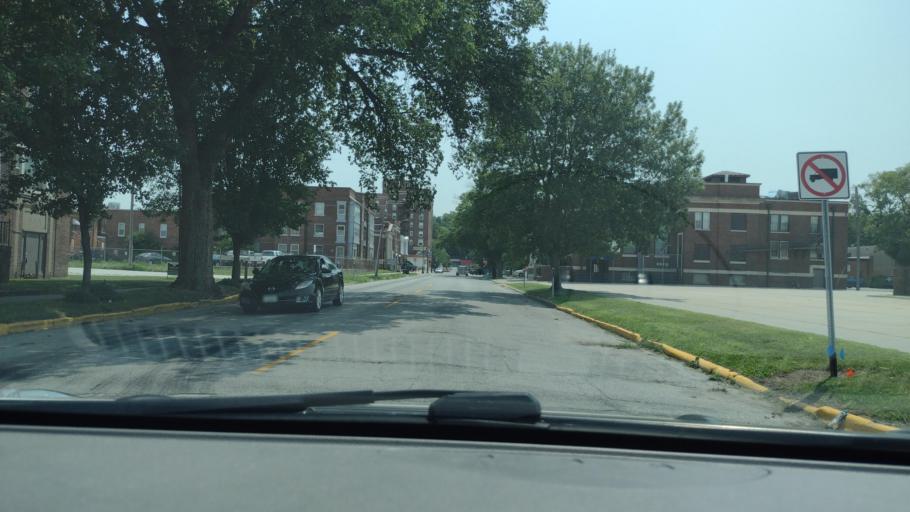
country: US
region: Iowa
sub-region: Pottawattamie County
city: Council Bluffs
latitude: 41.2602
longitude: -95.8540
